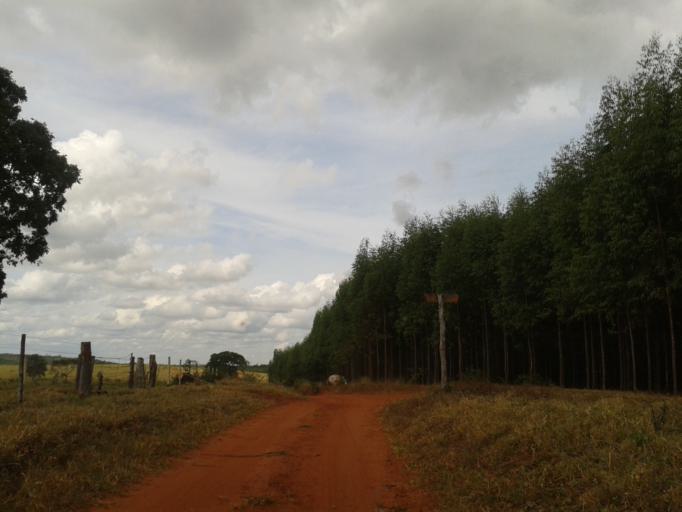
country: BR
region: Minas Gerais
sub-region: Campina Verde
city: Campina Verde
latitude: -19.4480
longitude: -49.6172
